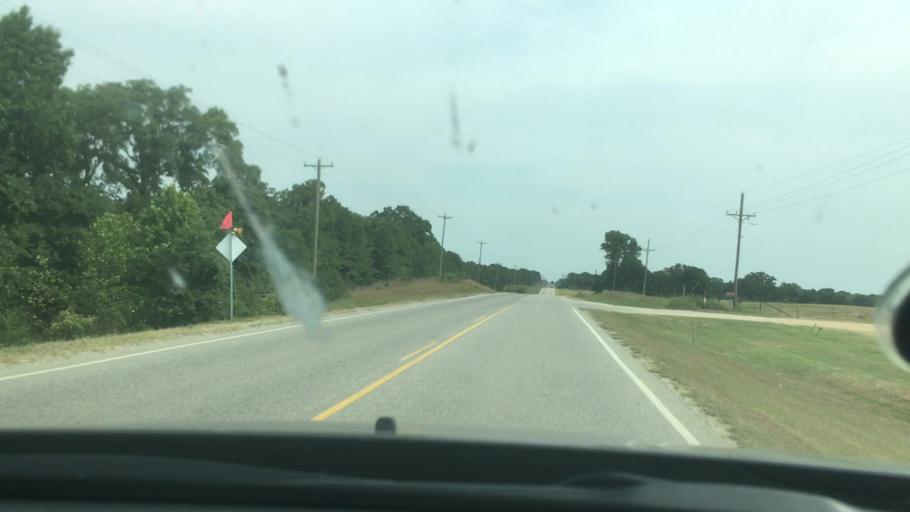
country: US
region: Oklahoma
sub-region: Bryan County
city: Durant
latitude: 34.2147
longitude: -96.4249
